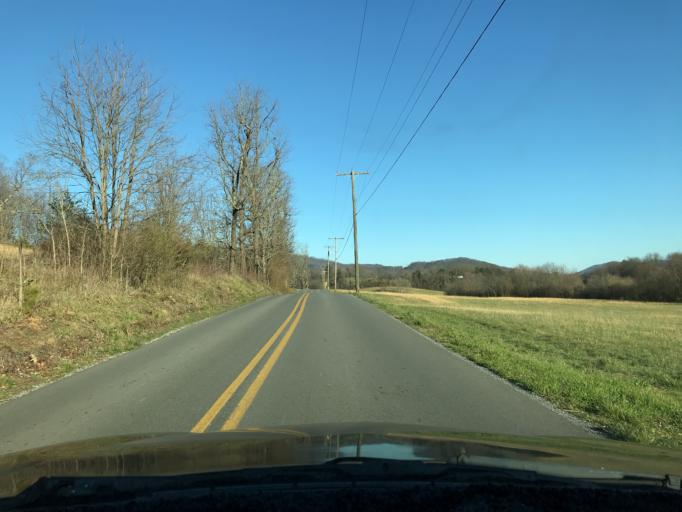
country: US
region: Virginia
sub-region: Botetourt County
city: Blue Ridge
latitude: 37.3903
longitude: -79.7253
